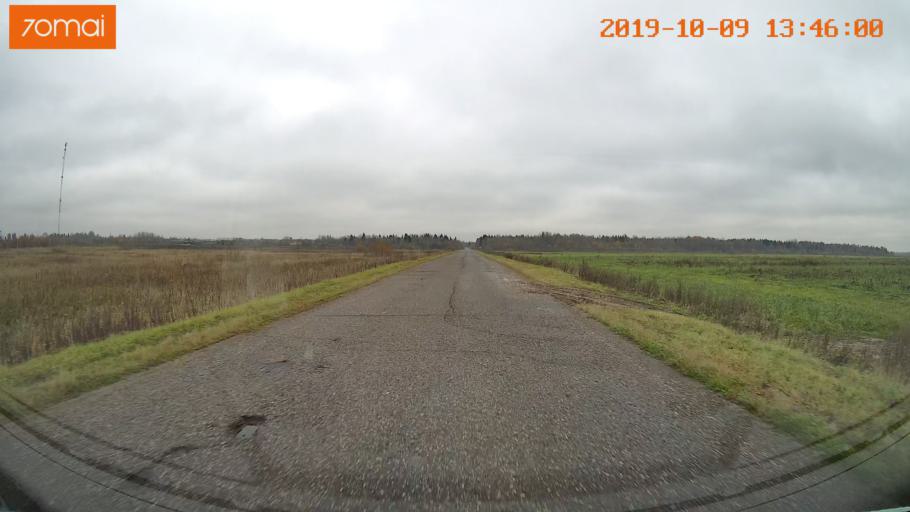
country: RU
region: Kostroma
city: Buy
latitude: 58.3796
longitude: 41.2145
